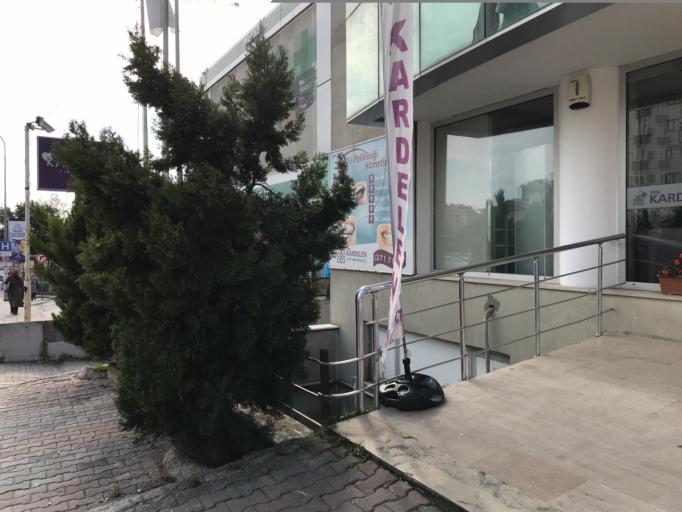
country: TR
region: Istanbul
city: Maltepe
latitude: 40.9405
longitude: 29.1428
